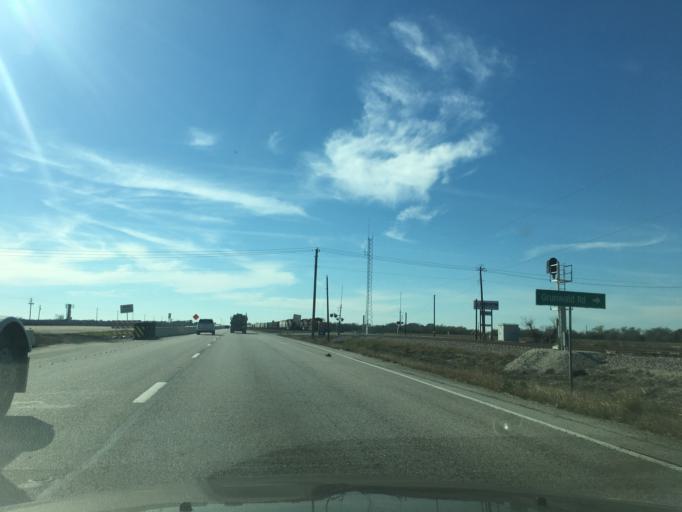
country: US
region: Texas
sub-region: Wharton County
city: East Bernard
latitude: 29.4784
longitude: -95.9490
